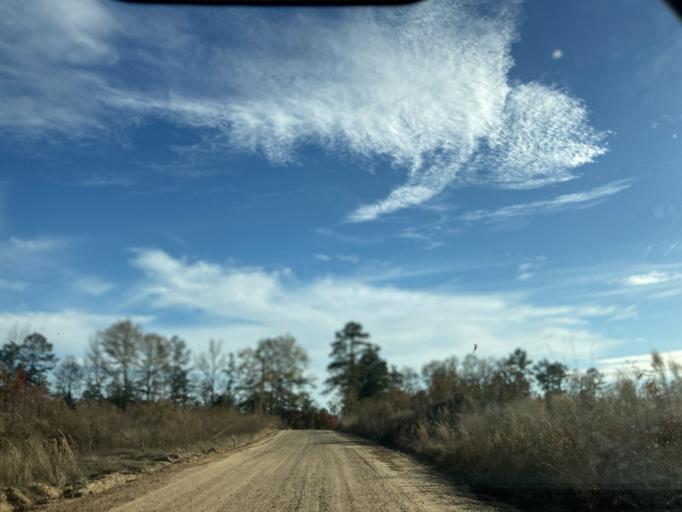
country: US
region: Georgia
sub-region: Jones County
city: Gray
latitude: 32.8926
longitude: -83.4886
